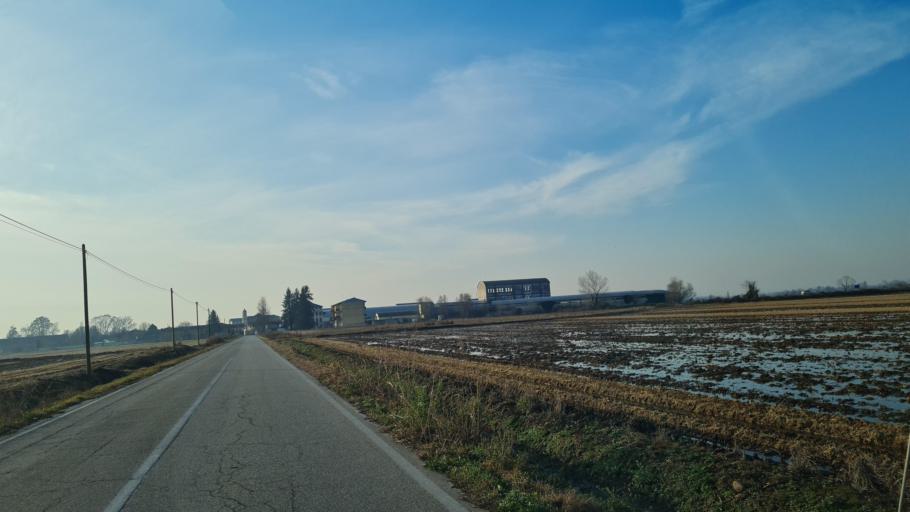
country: IT
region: Piedmont
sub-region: Provincia di Vercelli
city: Albano Vercellese
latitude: 45.4333
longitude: 8.3818
